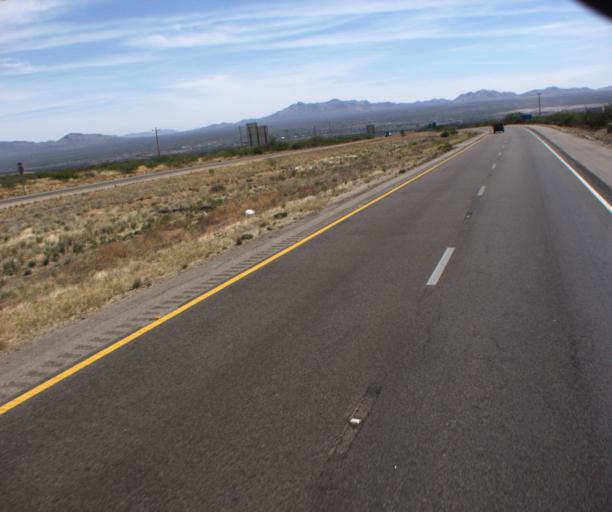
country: US
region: Arizona
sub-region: Cochise County
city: Whetstone
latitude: 31.9671
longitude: -110.3360
